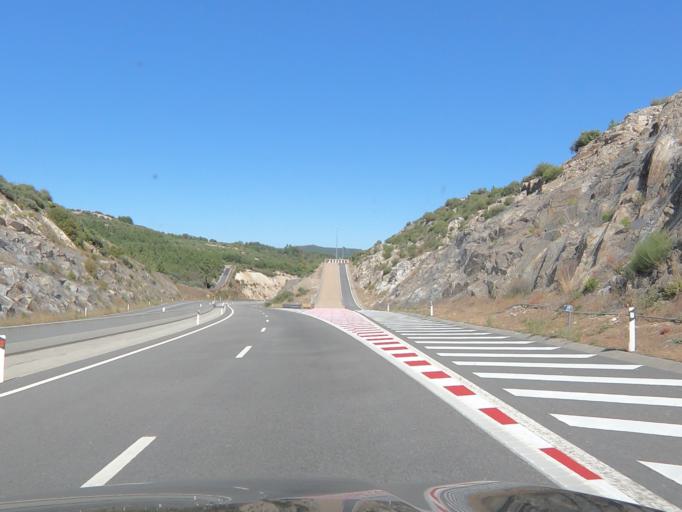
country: PT
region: Vila Real
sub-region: Murca
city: Murca
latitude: 41.3828
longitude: -7.4812
